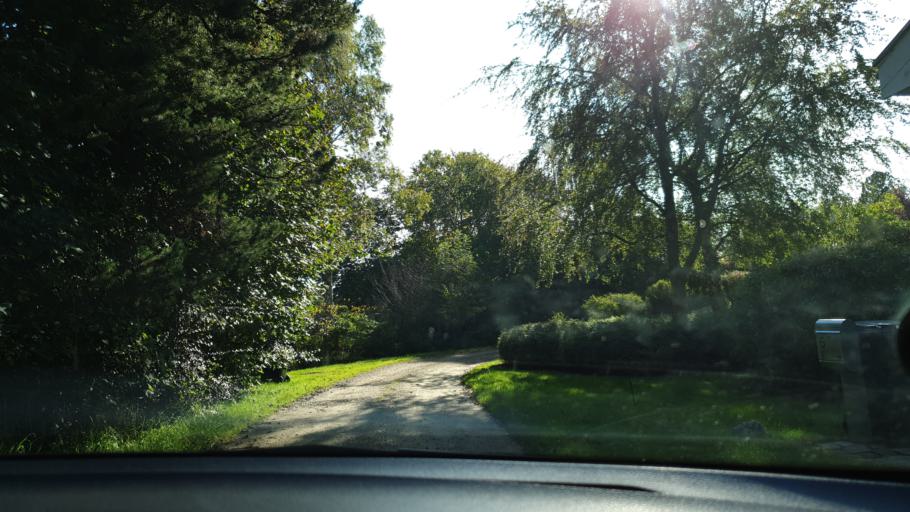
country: DK
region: Zealand
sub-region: Odsherred Kommune
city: Hojby
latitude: 55.9352
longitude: 11.6259
